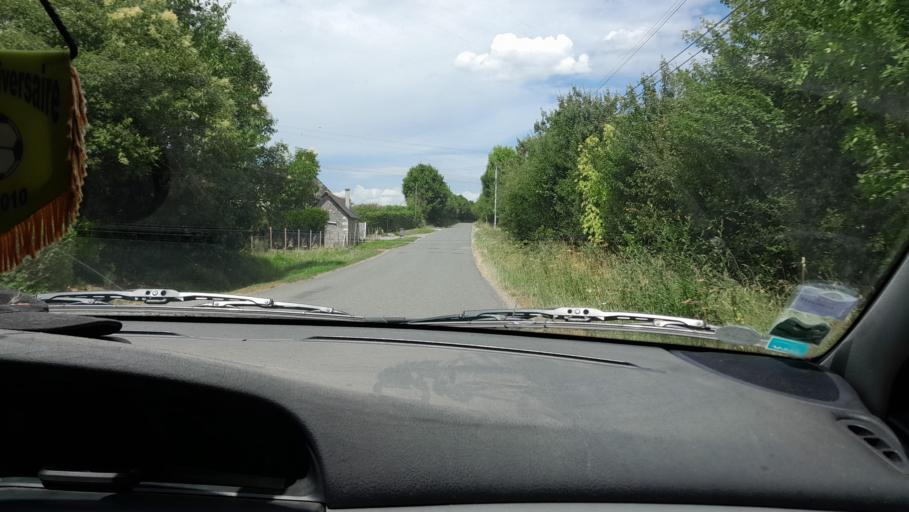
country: FR
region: Pays de la Loire
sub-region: Departement de la Mayenne
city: Saint-Pierre-la-Cour
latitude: 48.1454
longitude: -1.0313
